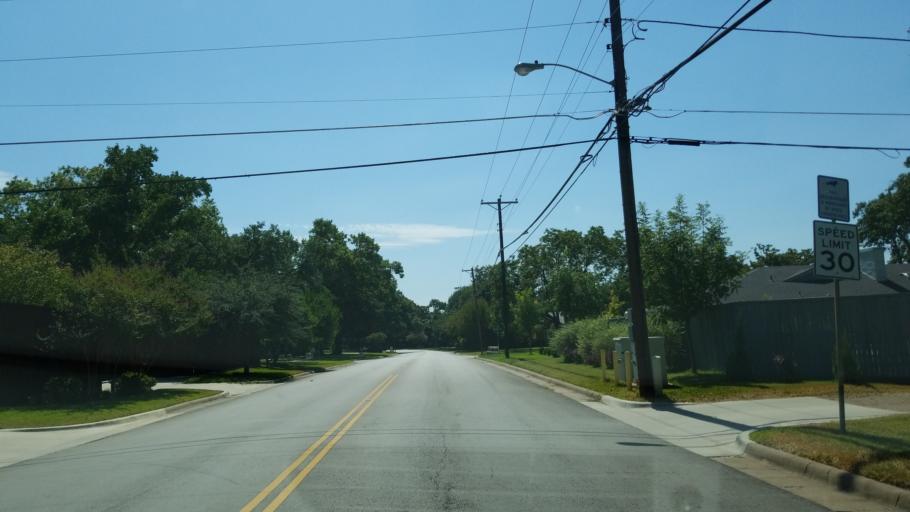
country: US
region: Texas
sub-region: Dallas County
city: Richardson
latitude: 32.9385
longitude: -96.7788
